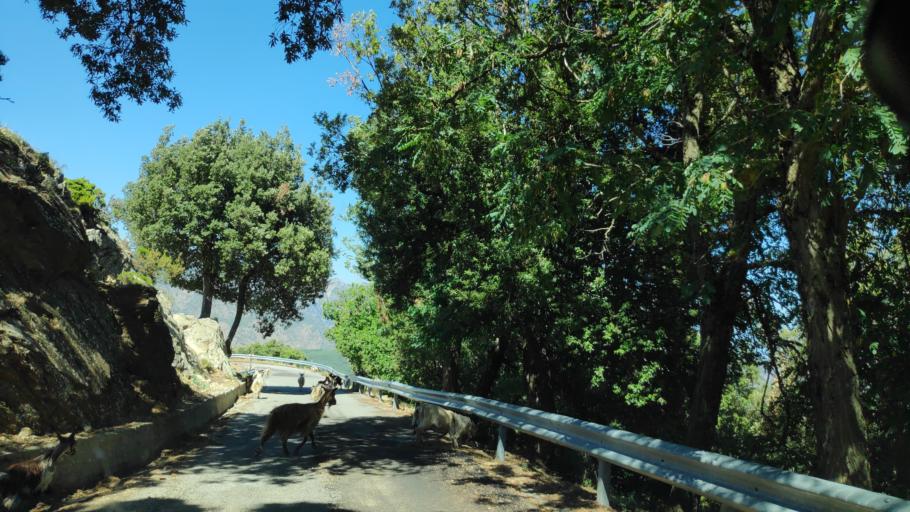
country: IT
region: Calabria
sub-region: Provincia di Reggio Calabria
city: Africo Vecchio
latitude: 38.0412
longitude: 15.9503
